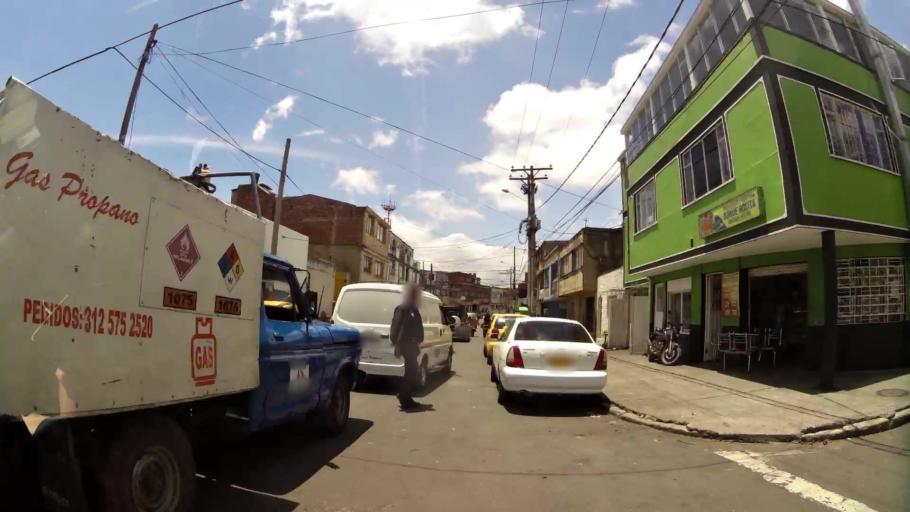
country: CO
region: Bogota D.C.
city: Bogota
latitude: 4.5942
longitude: -74.0942
